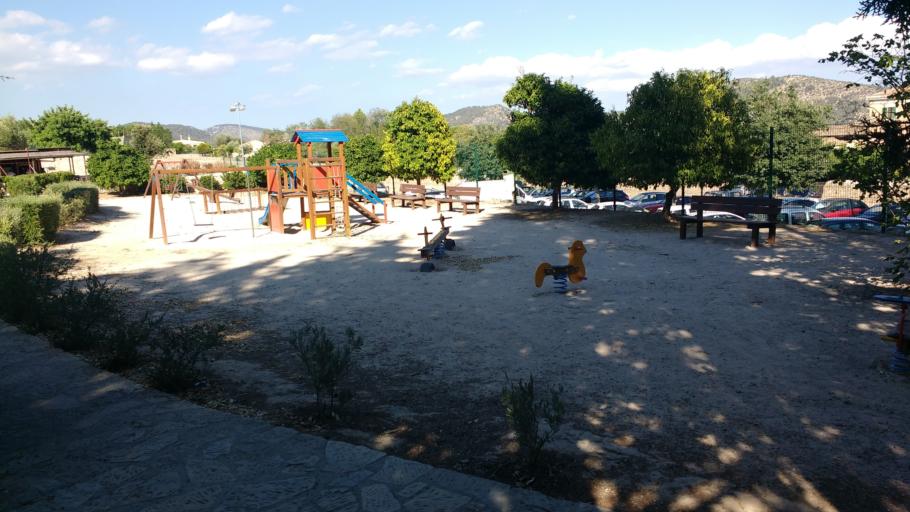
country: ES
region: Balearic Islands
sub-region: Illes Balears
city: Alaro
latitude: 39.7081
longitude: 2.7897
